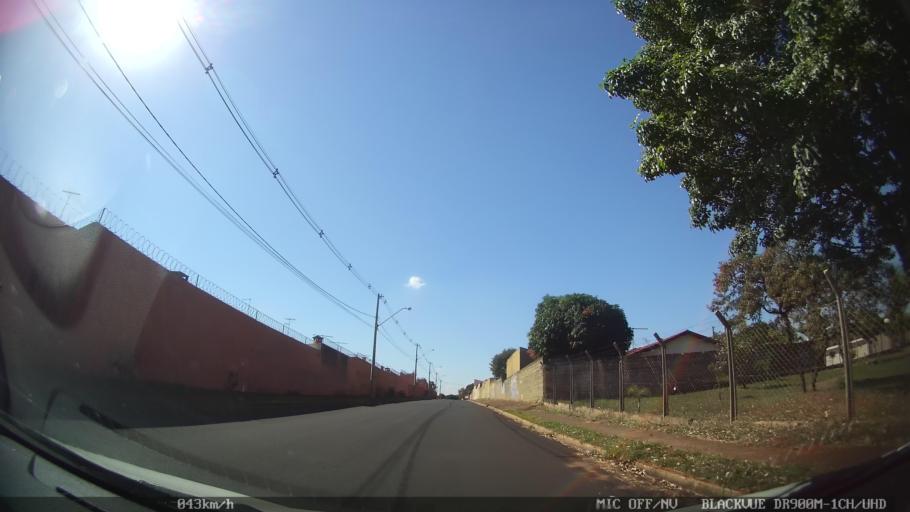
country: BR
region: Sao Paulo
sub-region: Ribeirao Preto
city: Ribeirao Preto
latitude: -21.2202
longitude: -47.7666
